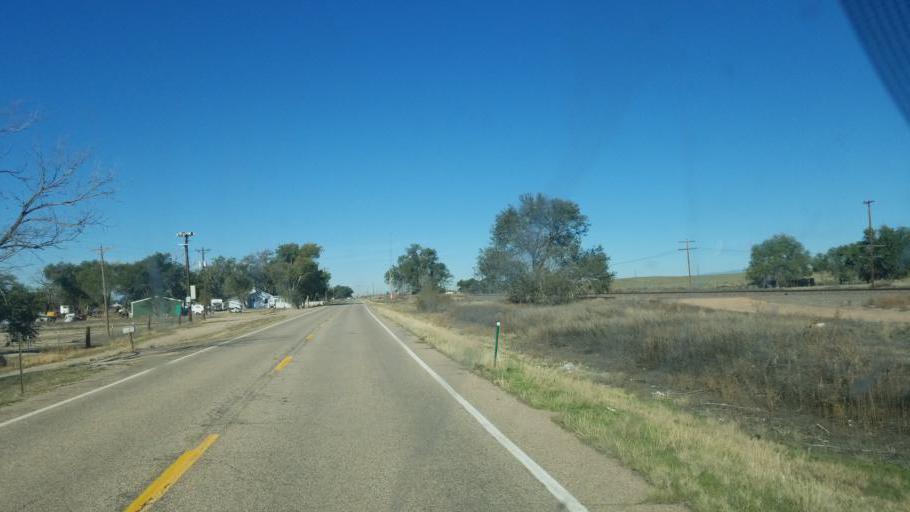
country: US
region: Colorado
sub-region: Pueblo County
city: Pueblo
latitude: 38.2601
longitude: -104.3413
